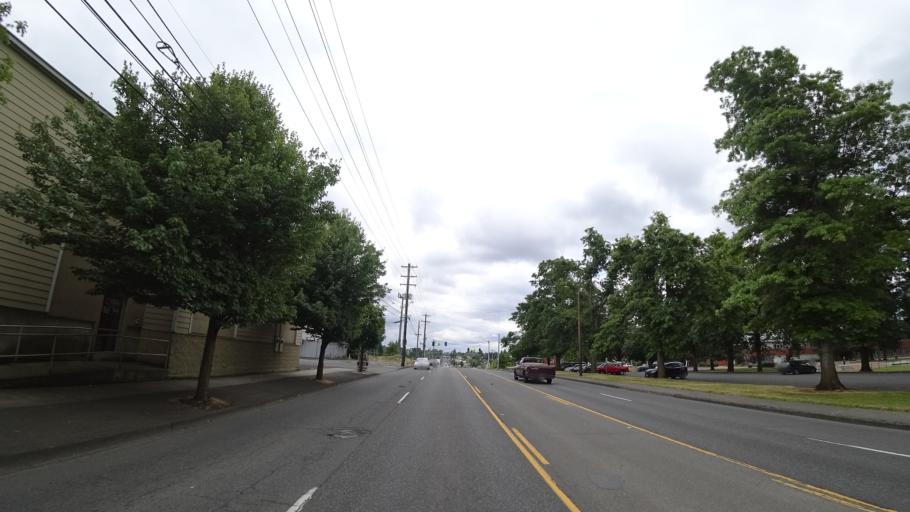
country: US
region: Oregon
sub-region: Multnomah County
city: Lents
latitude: 45.5431
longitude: -122.5778
